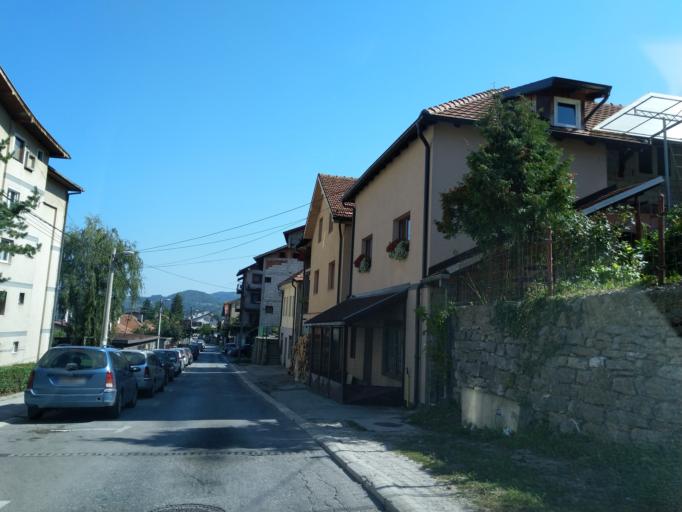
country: RS
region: Central Serbia
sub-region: Zlatiborski Okrug
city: Uzice
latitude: 43.8584
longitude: 19.8269
